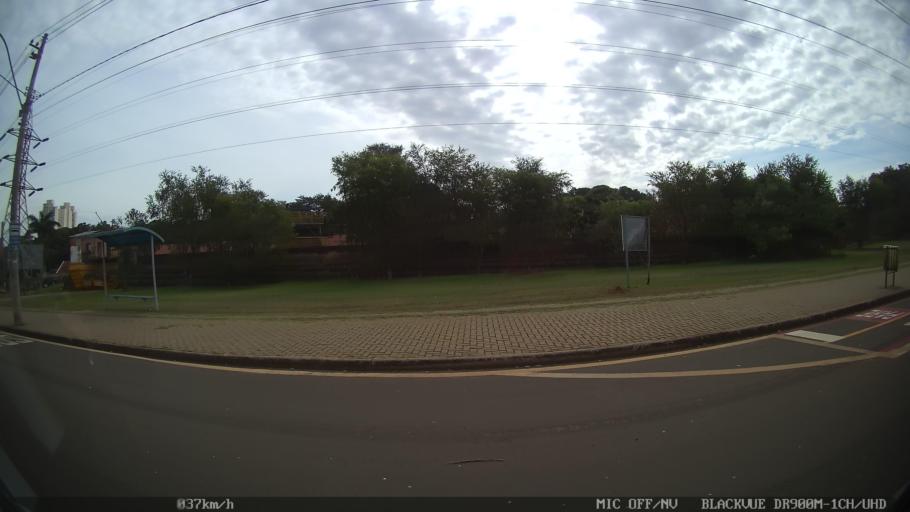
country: BR
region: Sao Paulo
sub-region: Piracicaba
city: Piracicaba
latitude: -22.7169
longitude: -47.6512
